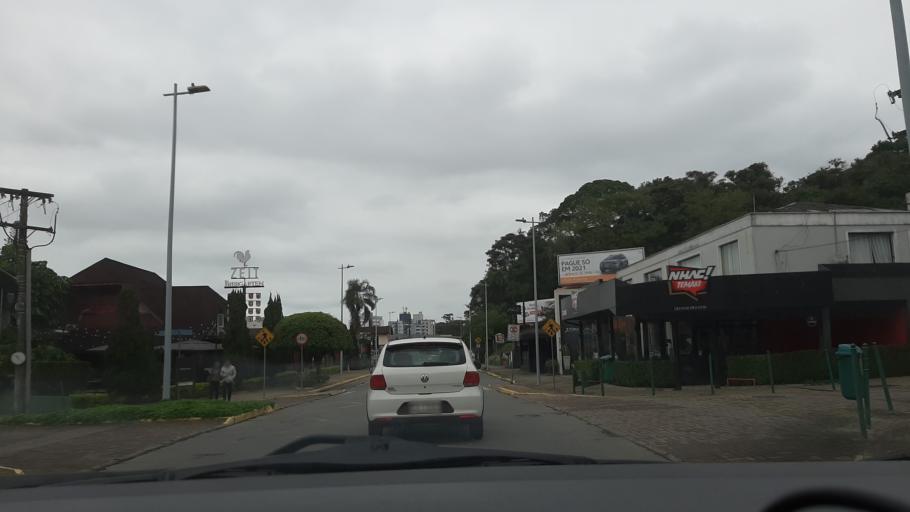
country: BR
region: Santa Catarina
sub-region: Joinville
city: Joinville
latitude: -26.3089
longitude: -48.8547
